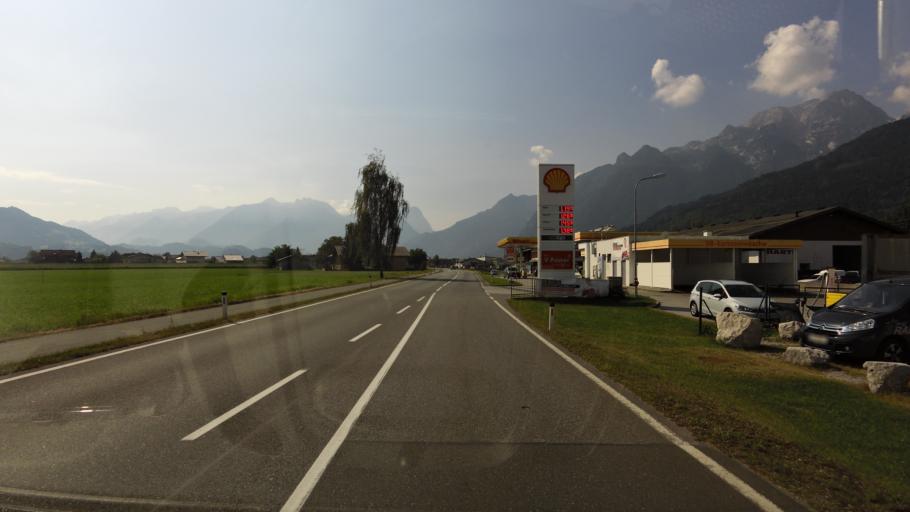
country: AT
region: Salzburg
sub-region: Politischer Bezirk Hallein
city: Kuchl
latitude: 47.6353
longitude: 13.1388
